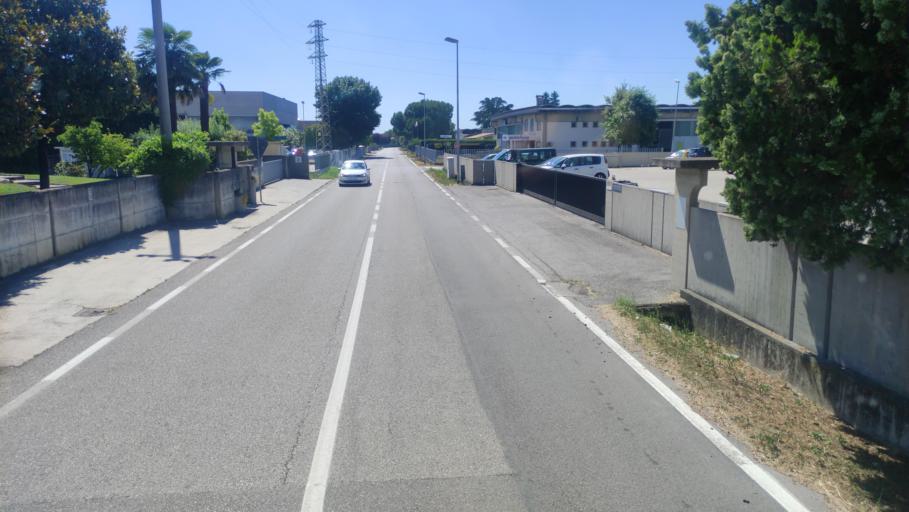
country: IT
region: Veneto
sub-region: Provincia di Treviso
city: Musano
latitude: 45.7397
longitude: 12.1187
